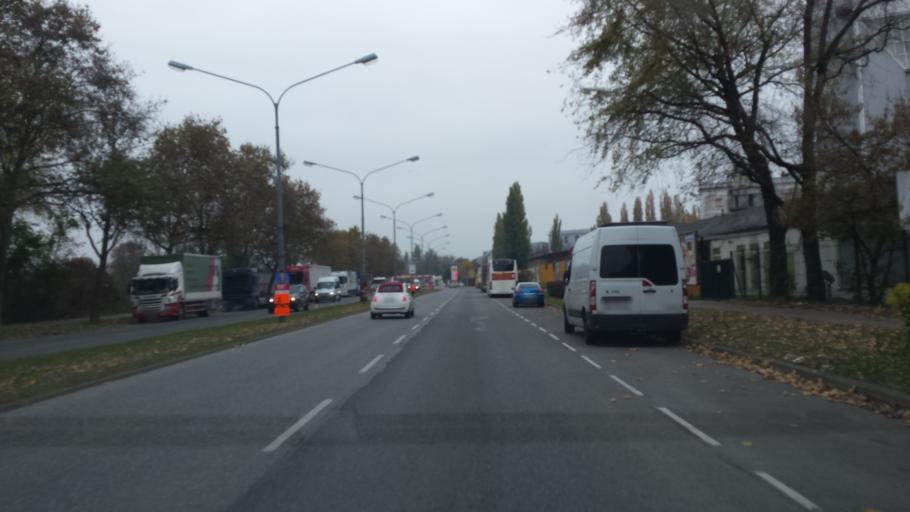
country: AT
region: Vienna
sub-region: Wien Stadt
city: Vienna
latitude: 48.2234
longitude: 16.4444
